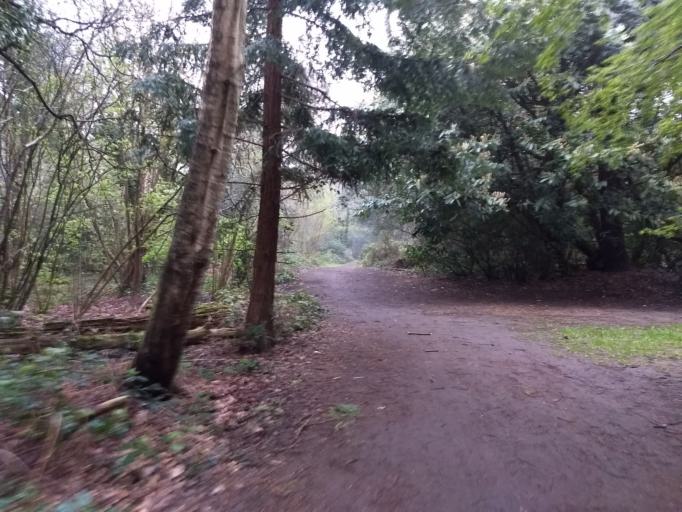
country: GB
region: England
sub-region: Dorset
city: Parkstone
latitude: 50.7218
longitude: -1.9205
